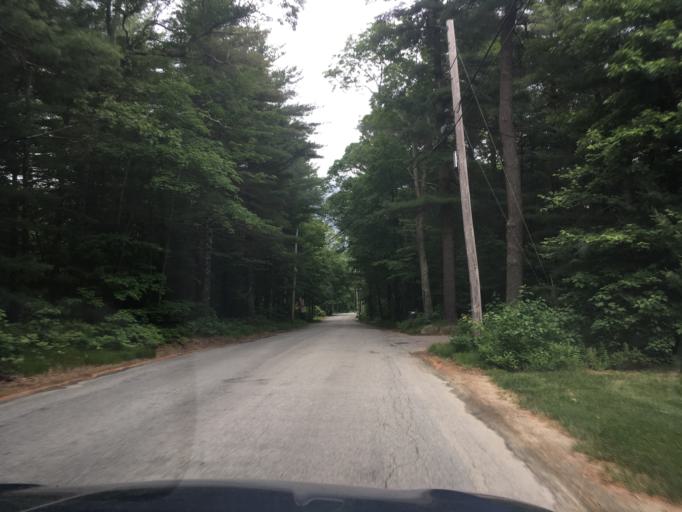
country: US
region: Rhode Island
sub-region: Washington County
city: Exeter
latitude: 41.6205
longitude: -71.5620
